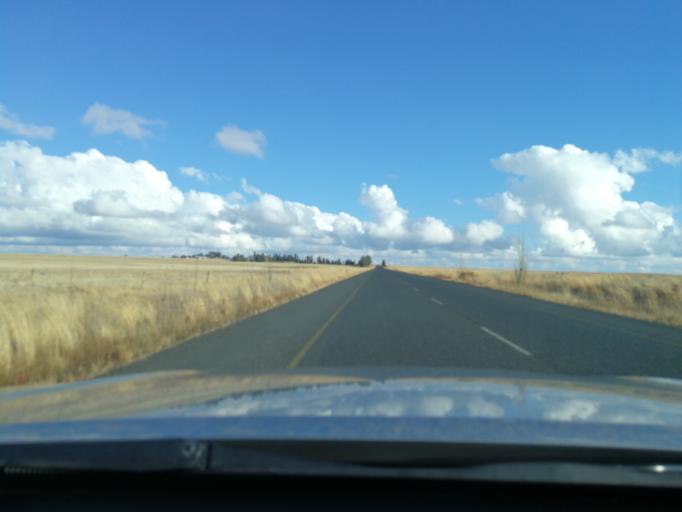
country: ZA
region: Orange Free State
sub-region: Thabo Mofutsanyana District Municipality
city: Bethlehem
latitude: -28.0559
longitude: 28.3646
